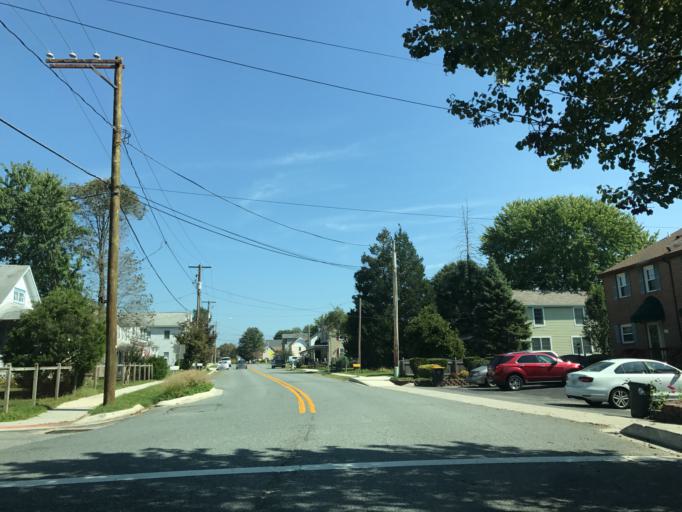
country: US
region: Maryland
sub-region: Cecil County
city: Elkton
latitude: 39.5299
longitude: -75.8073
